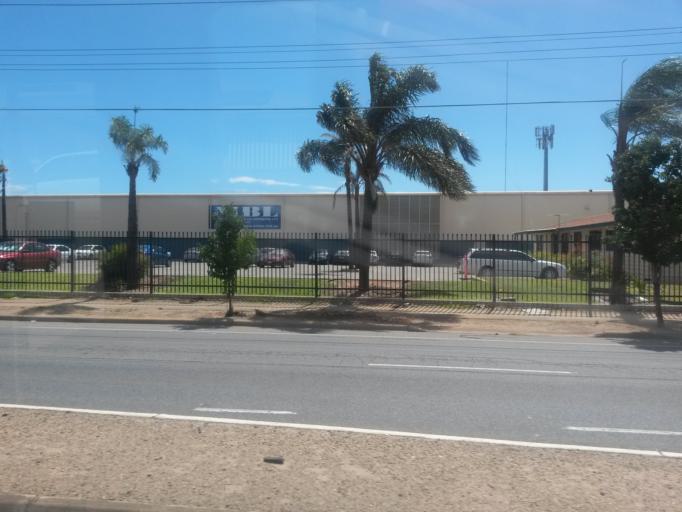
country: AU
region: South Australia
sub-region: Charles Sturt
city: Woodville North
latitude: -34.8549
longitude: 138.5470
